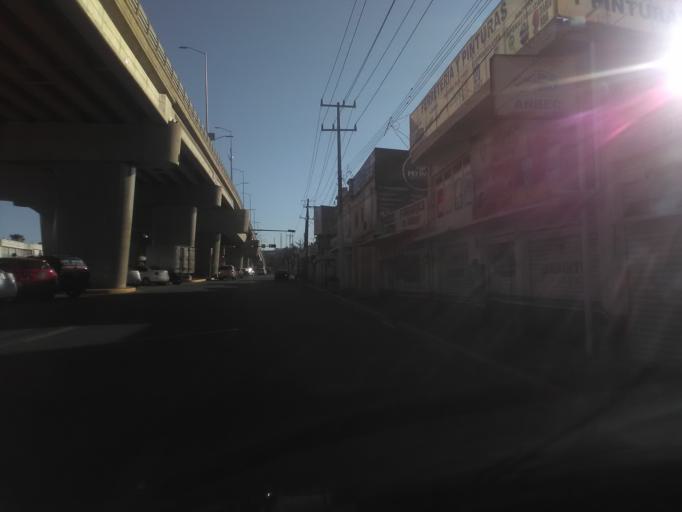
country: MX
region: Durango
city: Victoria de Durango
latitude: 24.0091
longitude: -104.6929
